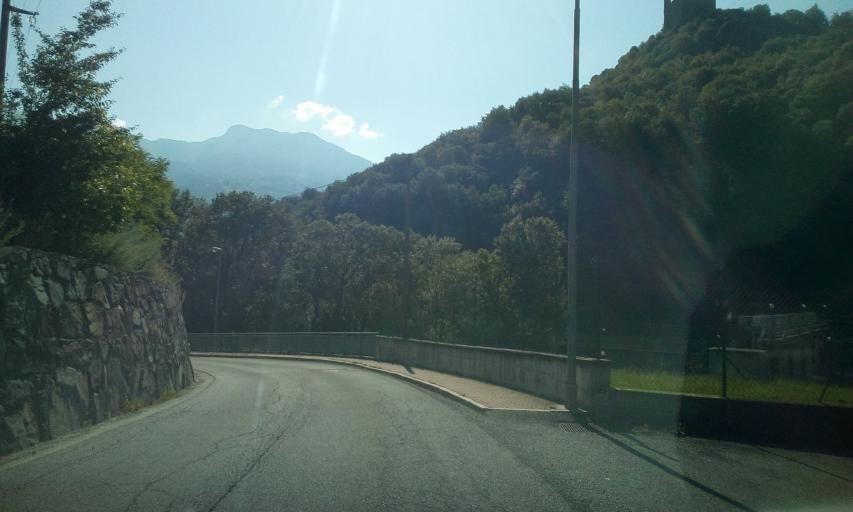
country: IT
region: Aosta Valley
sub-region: Valle d'Aosta
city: Chatillon
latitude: 45.7437
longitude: 7.6238
